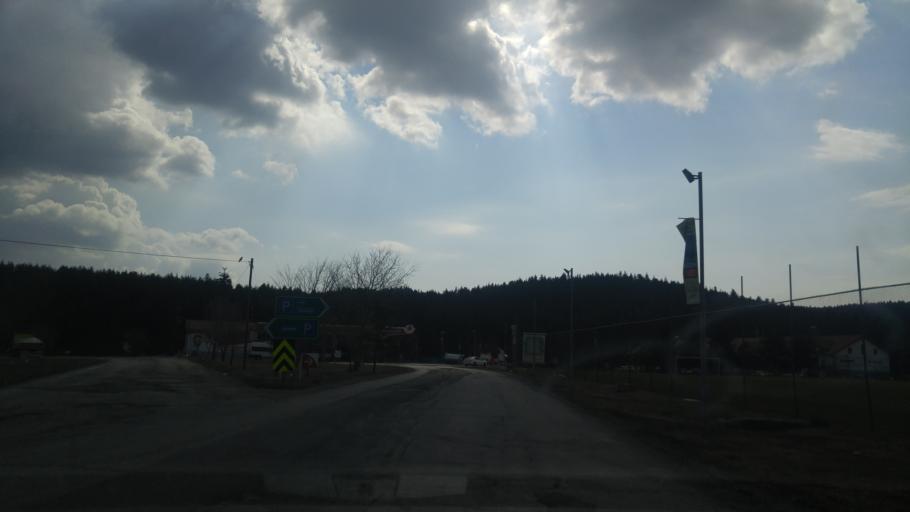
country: TR
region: Bolu
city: Gerede
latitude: 40.6099
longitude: 32.2520
